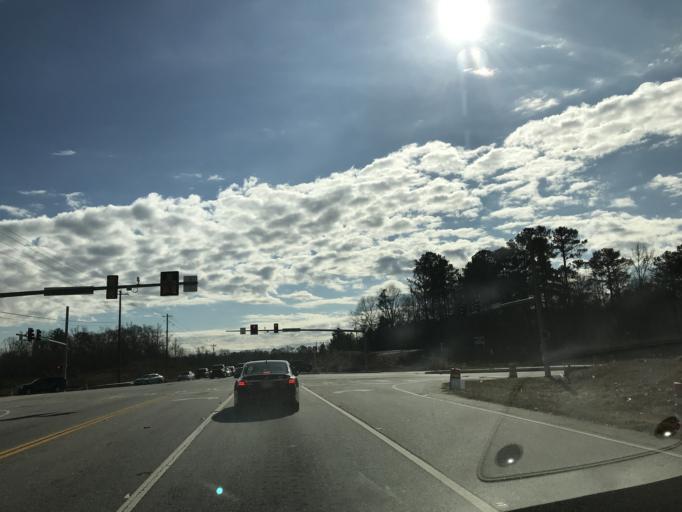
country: US
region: Georgia
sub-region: Paulding County
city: Hiram
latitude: 33.8572
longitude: -84.7587
